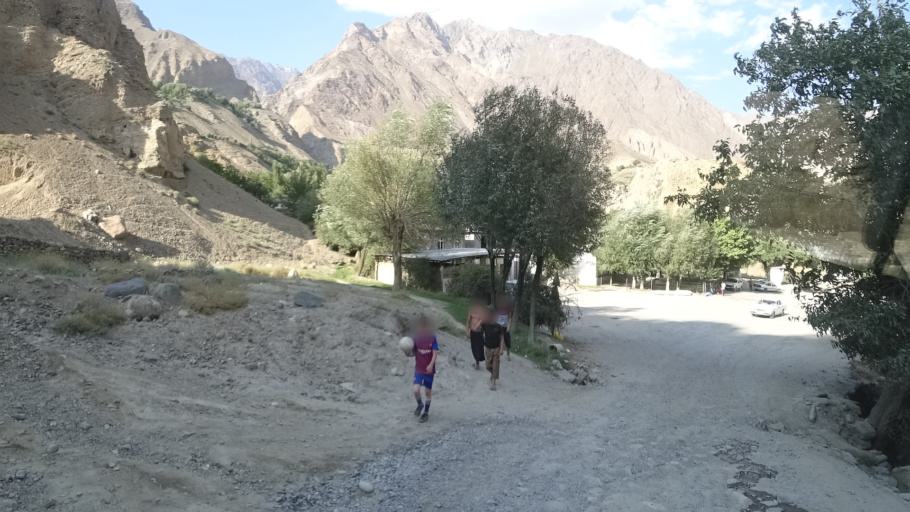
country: TJ
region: Gorno-Badakhshan
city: Vanj
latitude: 38.3161
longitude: 71.2711
